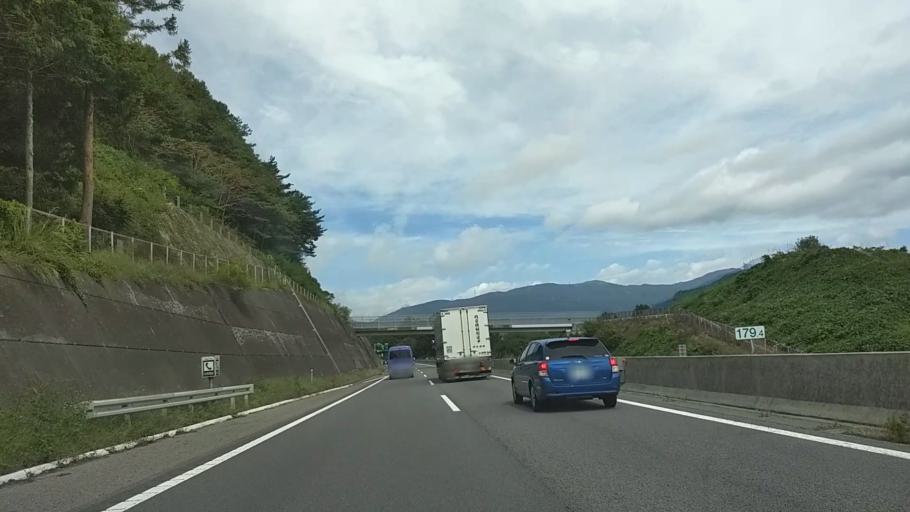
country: JP
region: Nagano
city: Okaya
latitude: 36.0361
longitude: 138.0638
